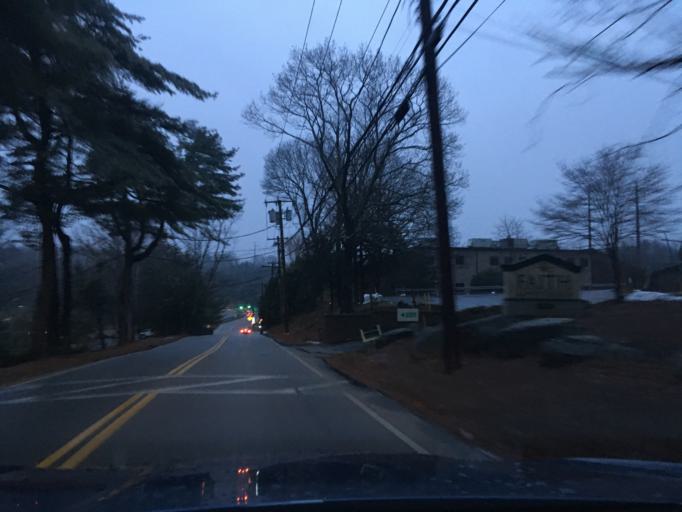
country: US
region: Rhode Island
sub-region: Kent County
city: West Warwick
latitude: 41.6990
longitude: -71.4791
